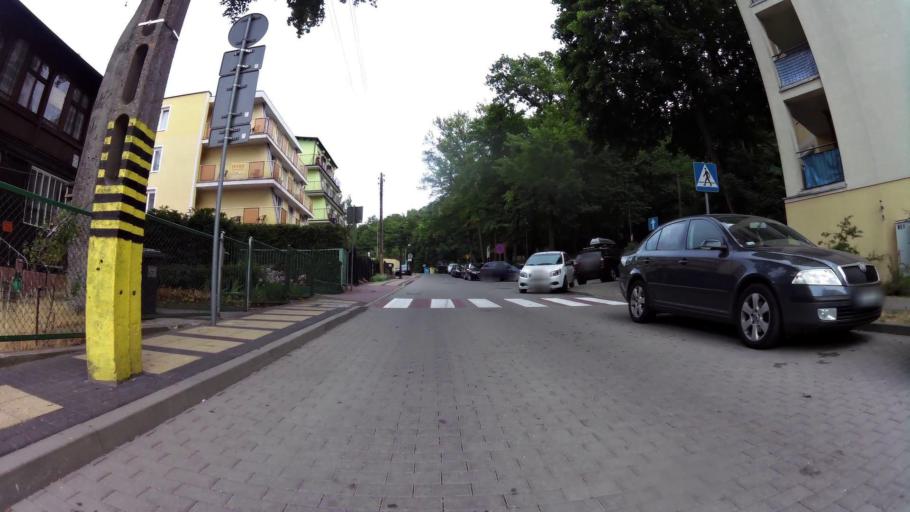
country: PL
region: West Pomeranian Voivodeship
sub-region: Powiat kamienski
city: Miedzyzdroje
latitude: 53.9340
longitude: 14.4577
